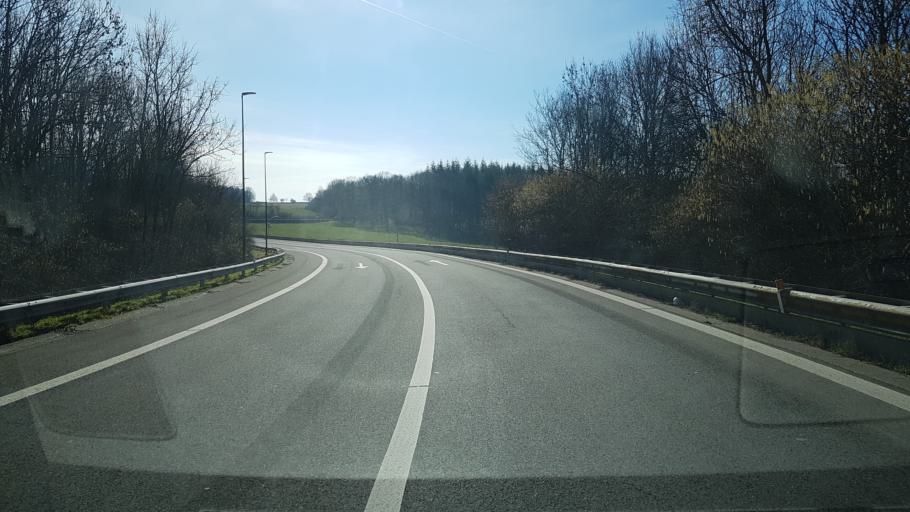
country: BE
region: Wallonia
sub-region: Province de Liege
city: Verviers
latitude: 50.5582
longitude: 5.8562
